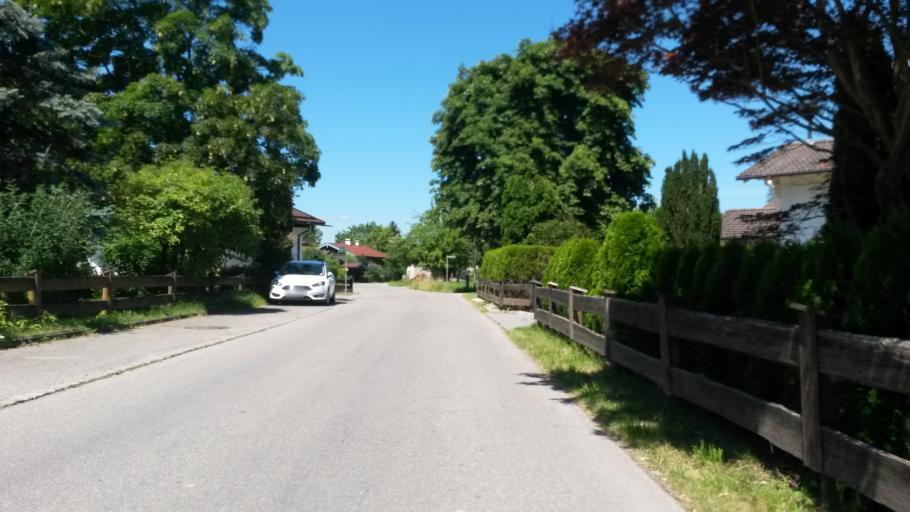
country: DE
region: Bavaria
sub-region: Upper Bavaria
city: Grassau
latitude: 47.7757
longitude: 12.4510
